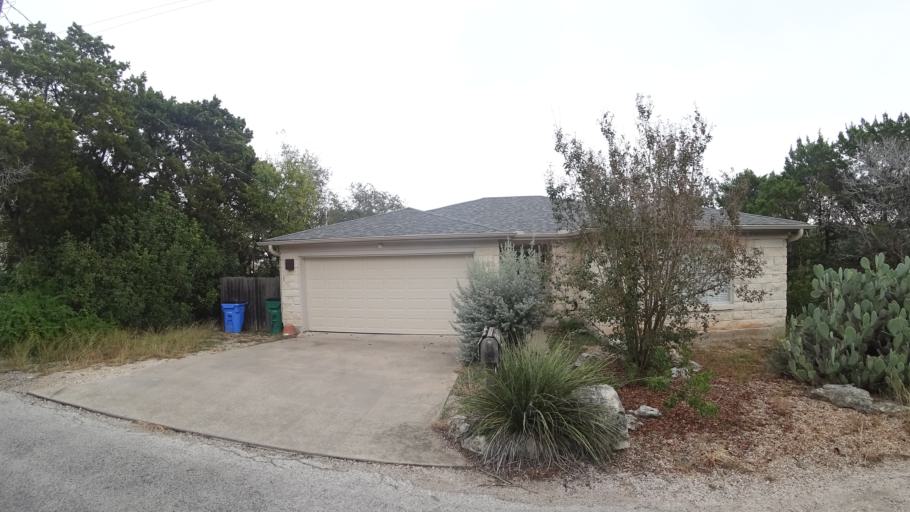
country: US
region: Texas
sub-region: Travis County
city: Hudson Bend
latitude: 30.3918
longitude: -97.9185
